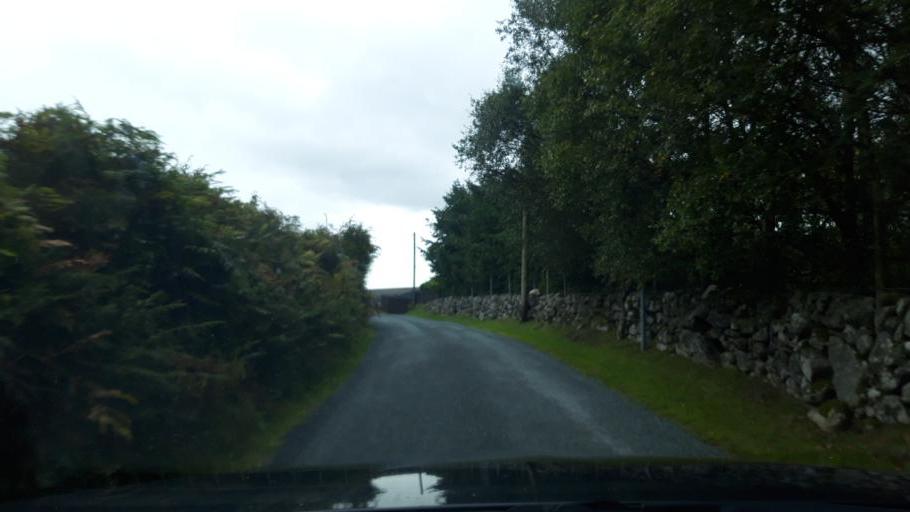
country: IE
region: Leinster
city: Ballinteer
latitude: 53.1791
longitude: -6.2641
